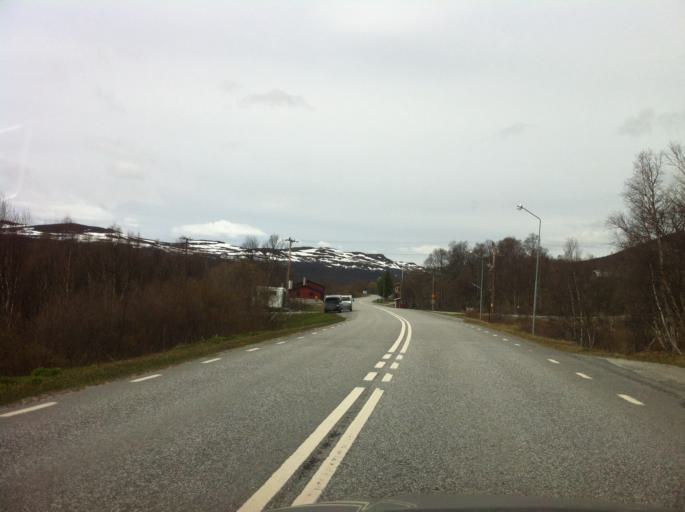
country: NO
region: Sor-Trondelag
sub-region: Tydal
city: Aas
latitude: 62.5483
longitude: 12.3192
